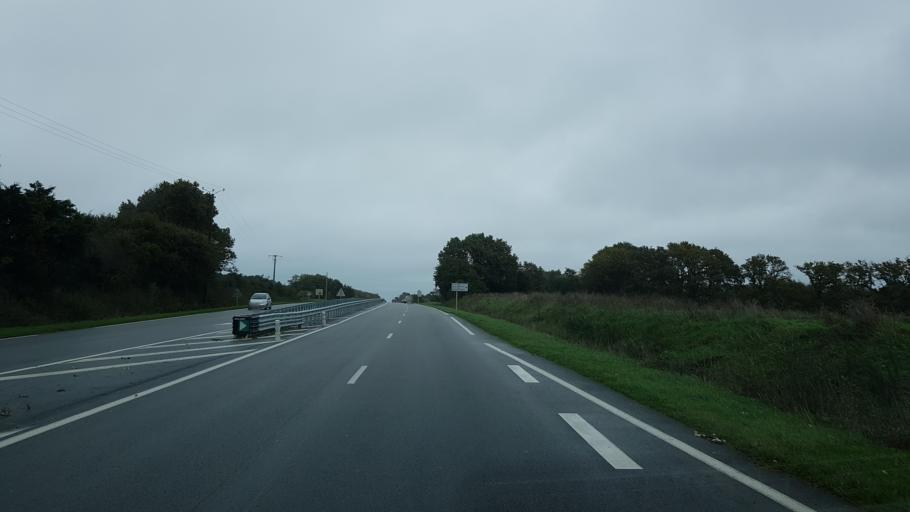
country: FR
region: Brittany
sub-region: Departement du Morbihan
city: Sarzeau
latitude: 47.5255
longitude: -2.7567
